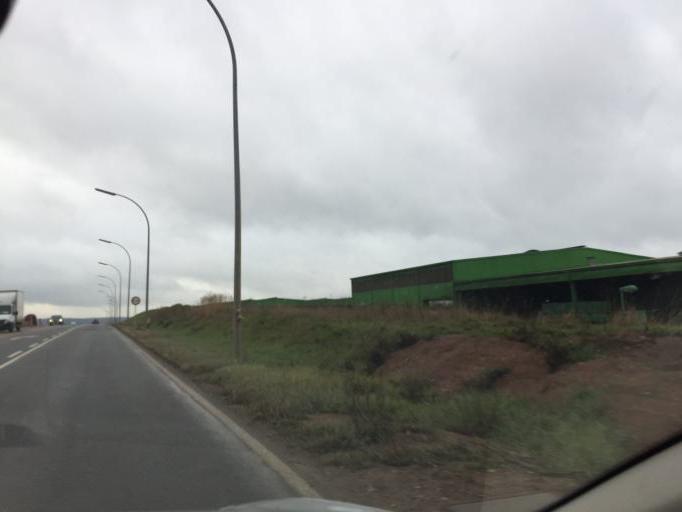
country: LU
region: Diekirch
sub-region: Canton de Diekirch
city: Diekirch
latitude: 49.8818
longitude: 6.1347
